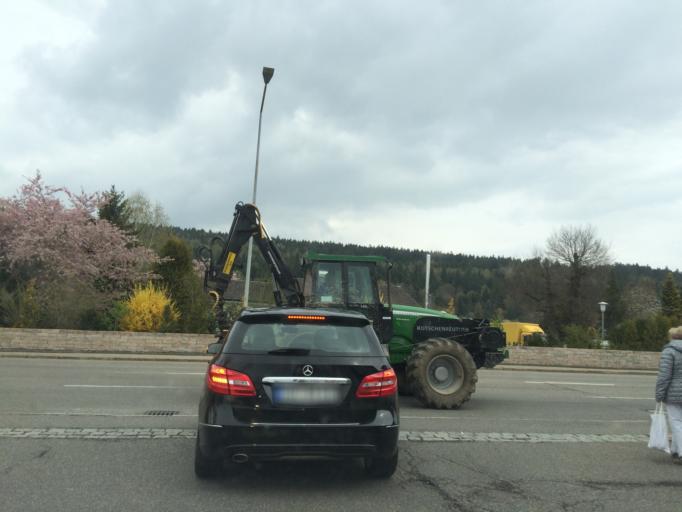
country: DE
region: Baden-Wuerttemberg
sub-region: Freiburg Region
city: Tuttlingen
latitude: 47.9810
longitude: 8.8447
